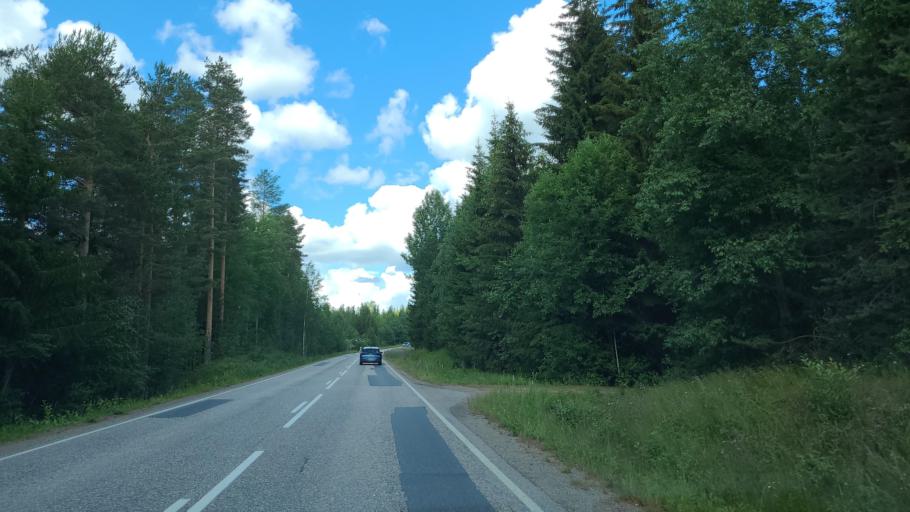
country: FI
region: Northern Savo
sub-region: Koillis-Savo
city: Kaavi
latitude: 62.9119
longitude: 28.7075
